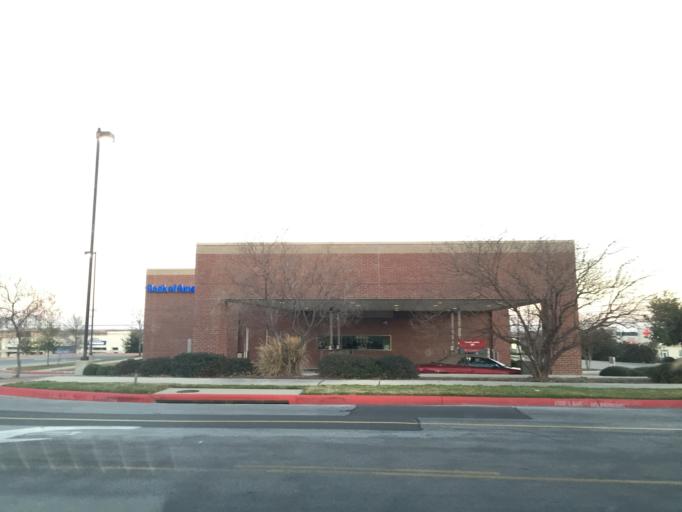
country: US
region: Texas
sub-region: Travis County
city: Pflugerville
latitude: 30.4523
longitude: -97.6054
